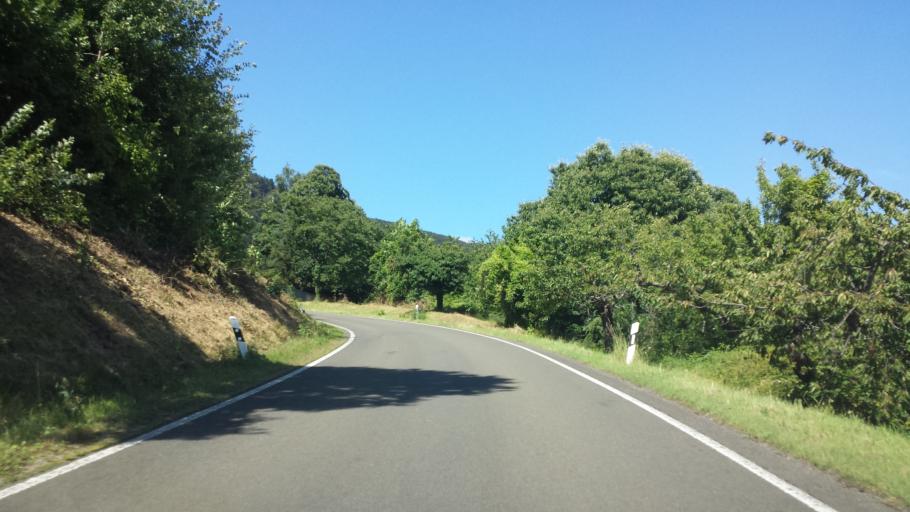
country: DE
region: Rheinland-Pfalz
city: Jakobsweiler
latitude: 49.6249
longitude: 7.9510
